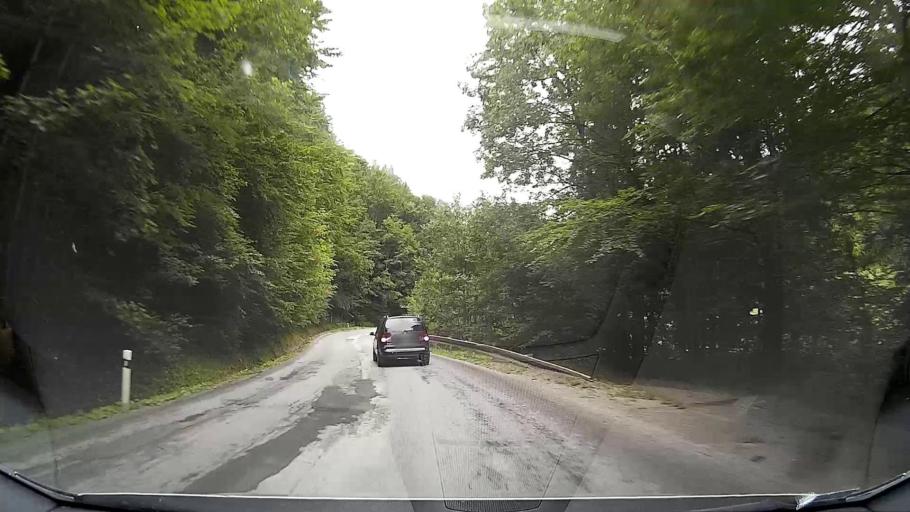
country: SK
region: Banskobystricky
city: Revuca
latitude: 48.7845
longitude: 20.1245
